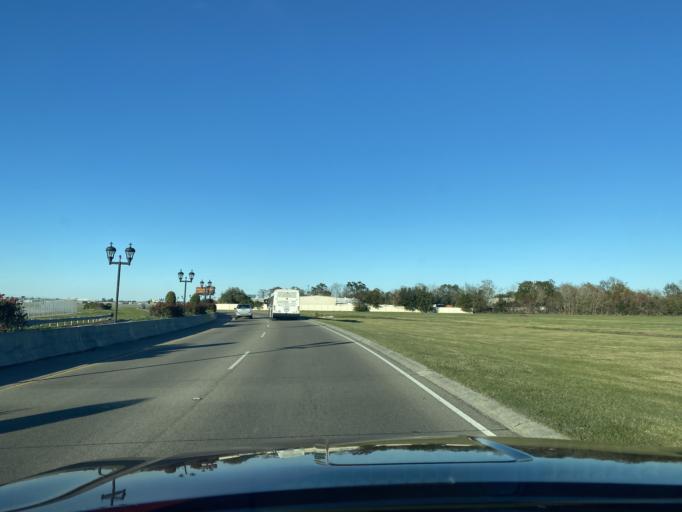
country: US
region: Louisiana
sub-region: Jefferson Parish
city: Kenner
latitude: 29.9882
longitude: -90.2480
